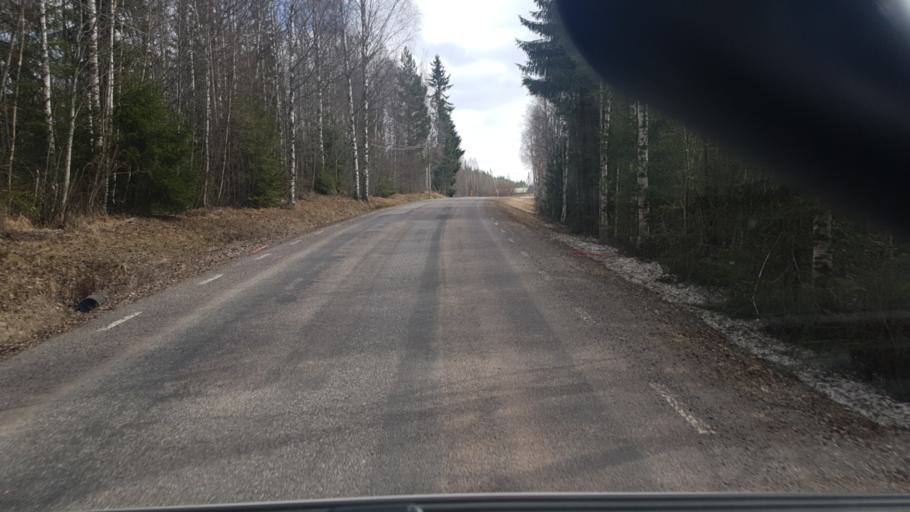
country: SE
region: Vaermland
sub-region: Eda Kommun
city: Amotfors
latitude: 59.8374
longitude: 12.4322
